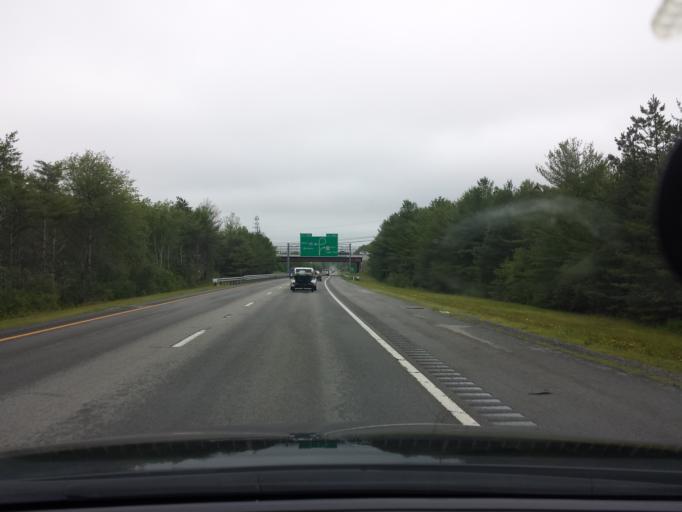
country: US
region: Massachusetts
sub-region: Plymouth County
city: Wareham Center
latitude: 41.7736
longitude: -70.7402
